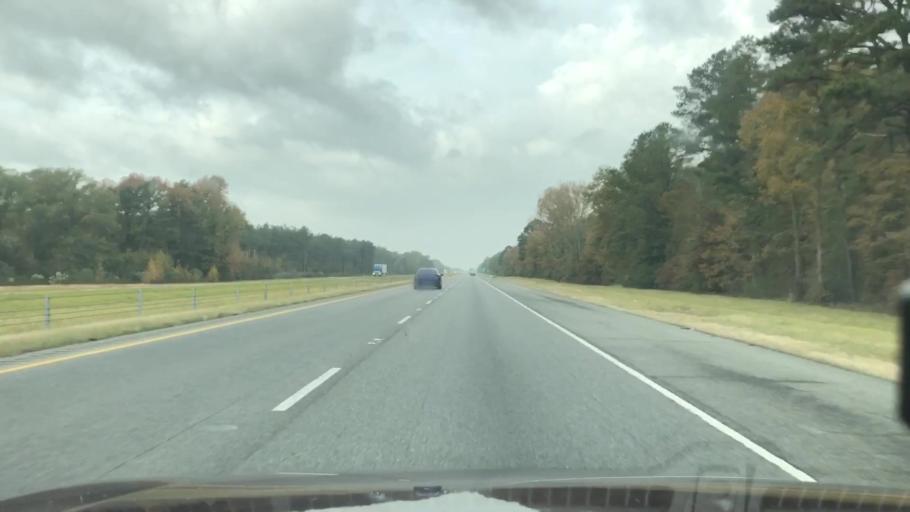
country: US
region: Louisiana
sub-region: Richland Parish
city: Delhi
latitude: 32.4469
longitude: -91.5508
